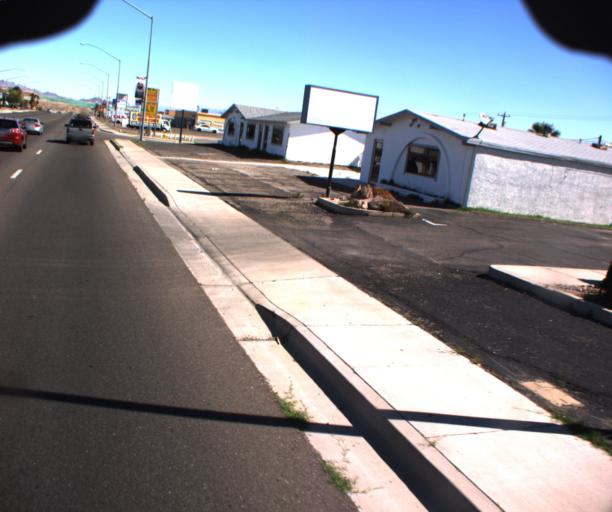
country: US
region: Arizona
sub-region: Mohave County
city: Bullhead City
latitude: 35.1103
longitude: -114.5980
